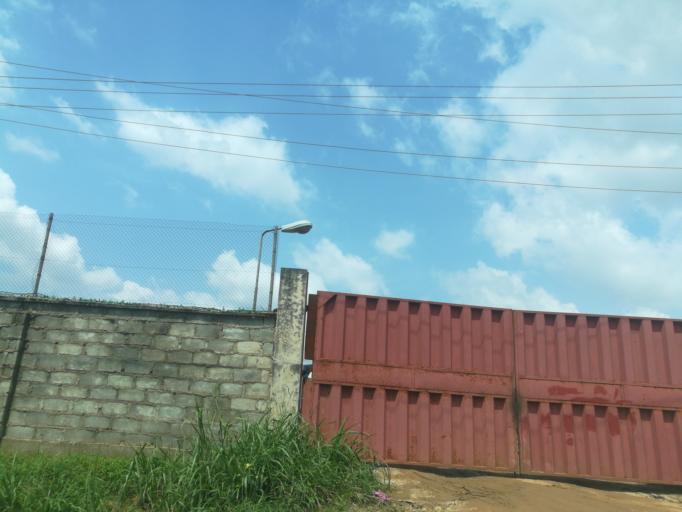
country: NG
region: Oyo
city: Ibadan
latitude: 7.3588
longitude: 3.8490
